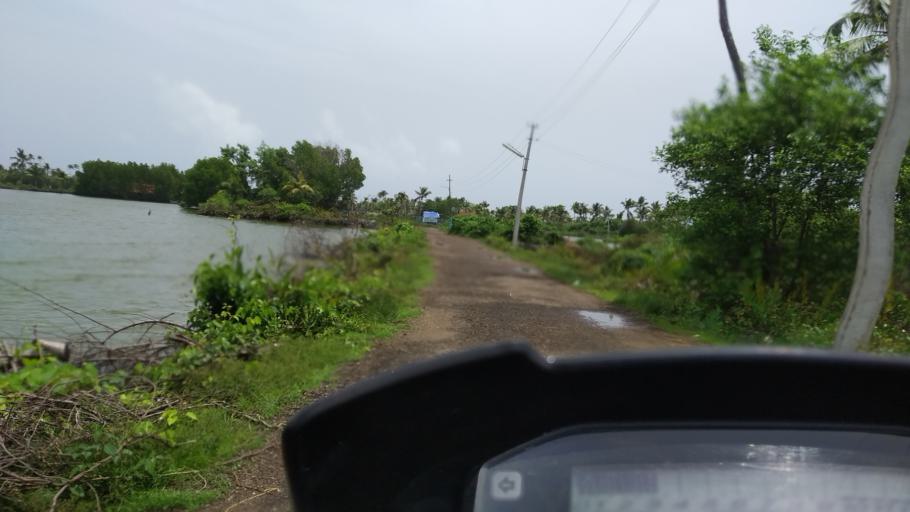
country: IN
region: Kerala
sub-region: Ernakulam
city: Elur
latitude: 10.0642
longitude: 76.2047
